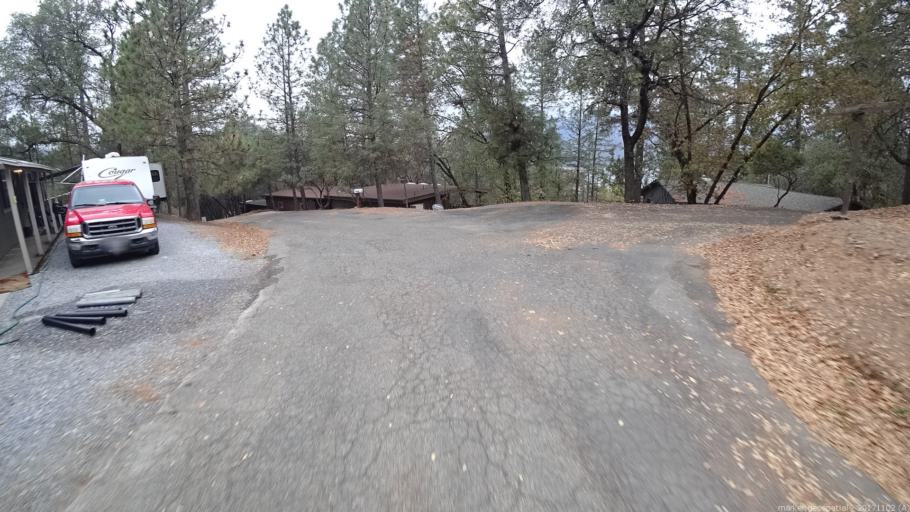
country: US
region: California
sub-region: Shasta County
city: Bella Vista
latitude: 40.7465
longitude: -122.2358
